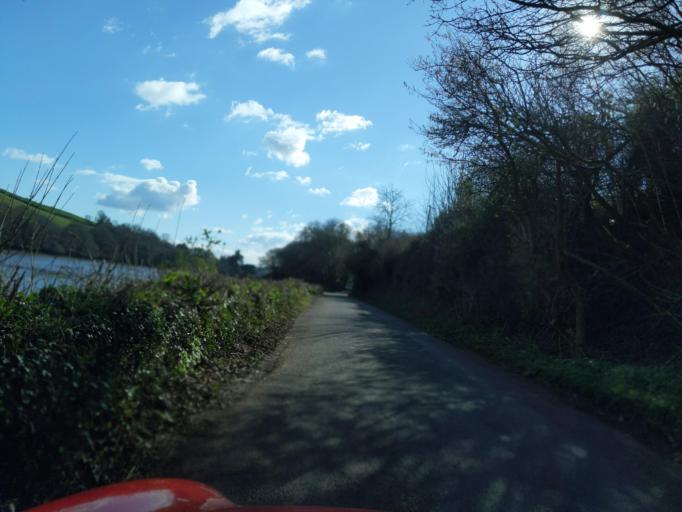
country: GB
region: England
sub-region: Devon
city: Kingsbridge
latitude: 50.2798
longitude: -3.7605
